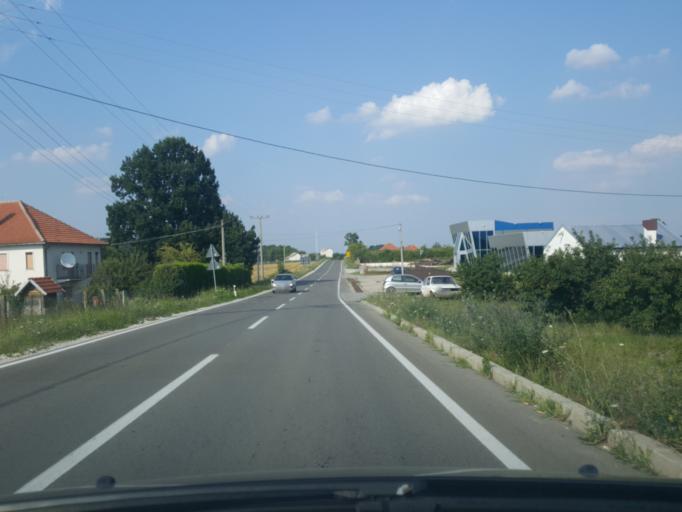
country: RS
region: Central Serbia
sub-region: Sumadijski Okrug
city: Topola
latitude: 44.2267
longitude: 20.6742
